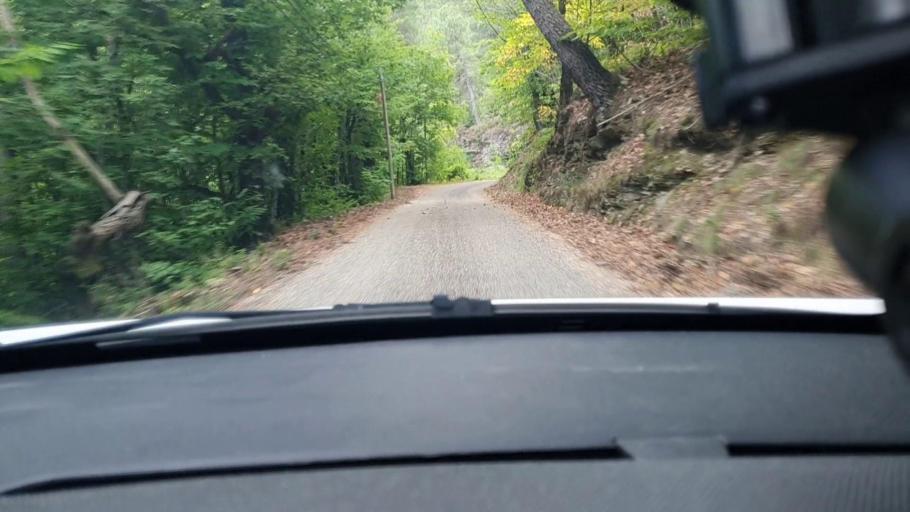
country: FR
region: Languedoc-Roussillon
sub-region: Departement du Gard
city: Branoux-les-Taillades
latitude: 44.2207
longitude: 3.9649
